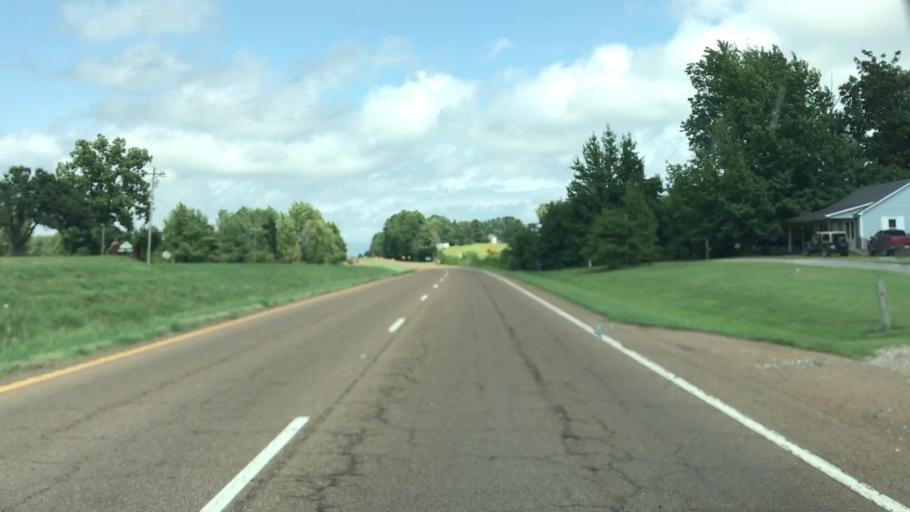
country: US
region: Tennessee
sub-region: Obion County
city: Englewood
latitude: 36.3530
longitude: -89.1412
